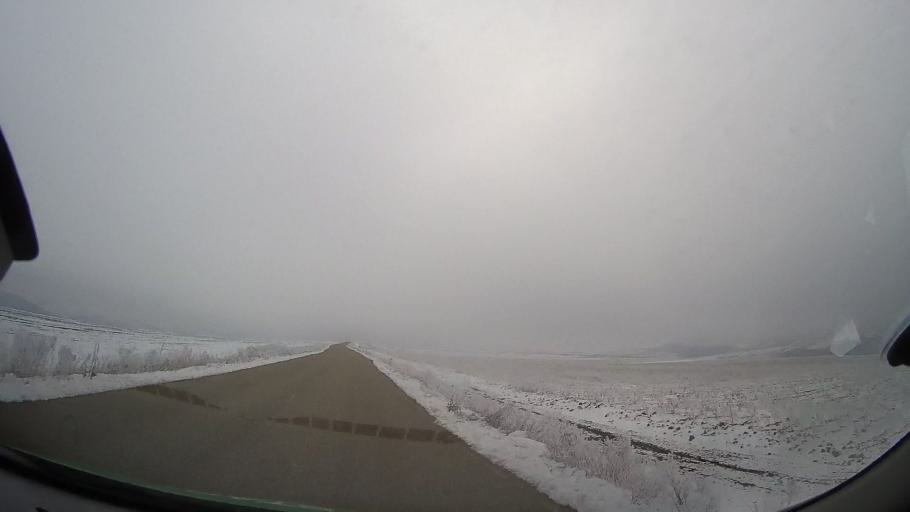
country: RO
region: Vaslui
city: Coroiesti
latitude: 46.2267
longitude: 27.4783
